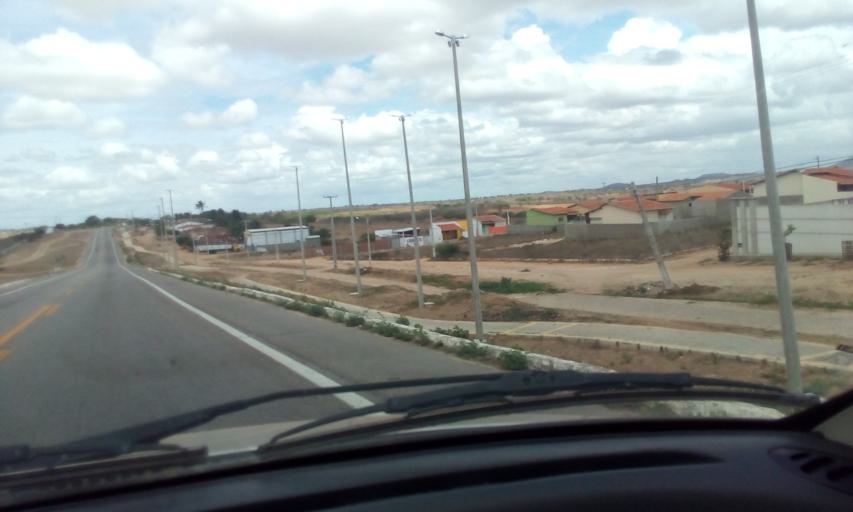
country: BR
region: Rio Grande do Norte
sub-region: Tangara
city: Tangara
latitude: -6.1944
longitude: -35.7946
